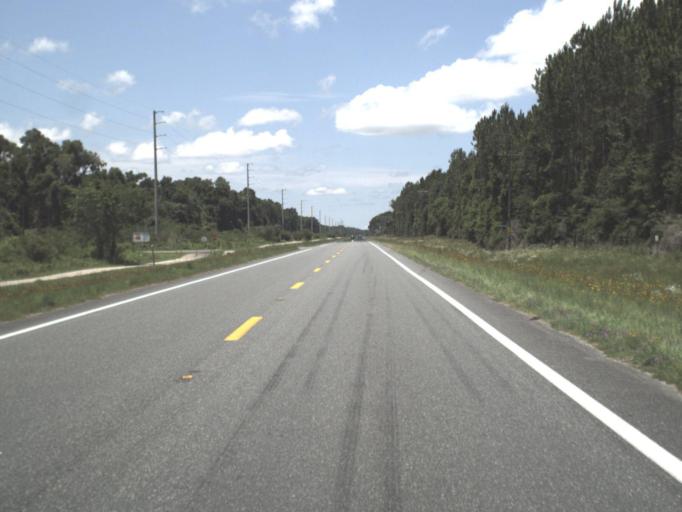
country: US
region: Florida
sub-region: Alachua County
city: High Springs
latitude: 29.9528
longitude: -82.8172
